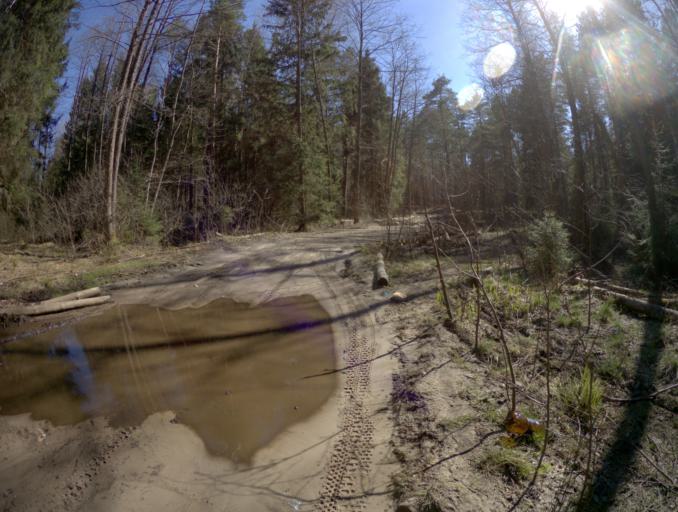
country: RU
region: Vladimir
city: Ivanishchi
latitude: 55.7880
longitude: 40.4284
